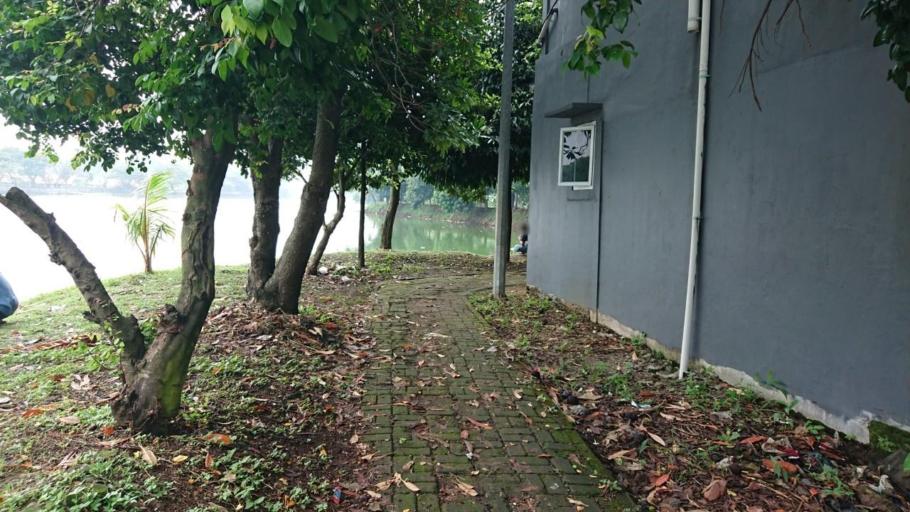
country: ID
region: West Java
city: Depok
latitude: -6.3574
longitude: 106.8683
